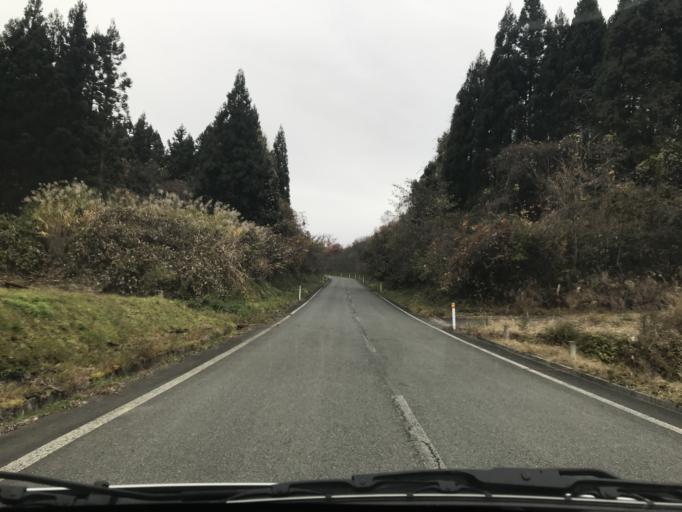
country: JP
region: Iwate
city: Ichinoseki
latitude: 39.0141
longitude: 141.0749
